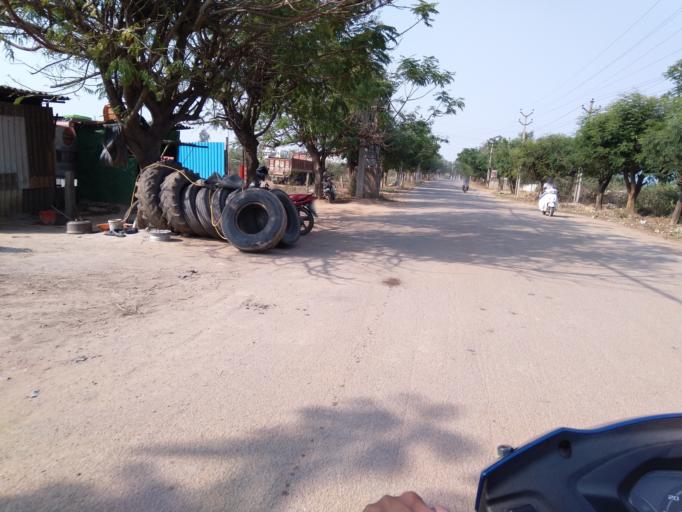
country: IN
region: Telangana
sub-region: Rangareddi
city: Quthbullapur
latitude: 17.5858
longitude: 78.4192
